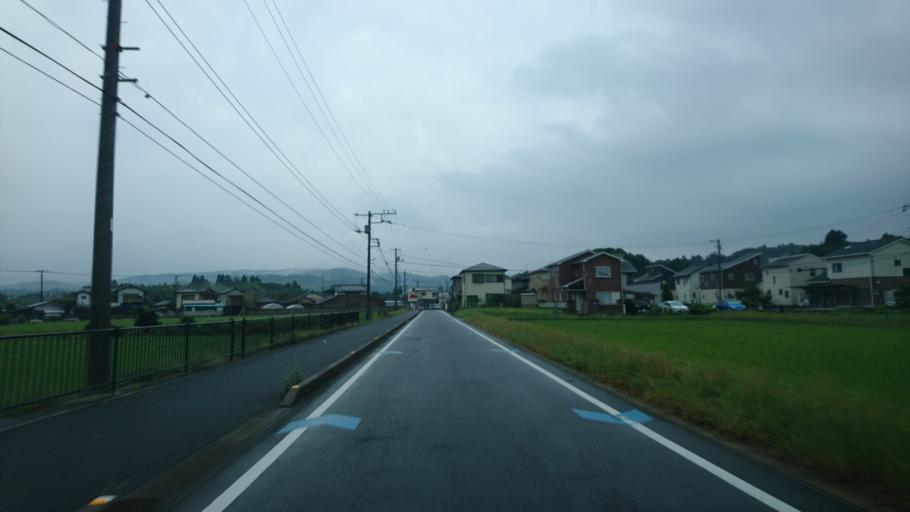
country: JP
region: Chiba
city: Kimitsu
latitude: 35.3012
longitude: 139.9720
